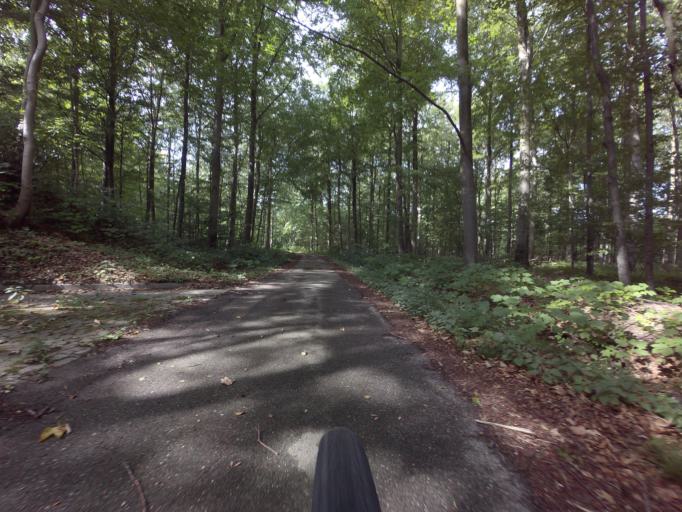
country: DK
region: Zealand
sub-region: Faxe Kommune
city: Fakse Ladeplads
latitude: 55.2357
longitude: 12.1897
